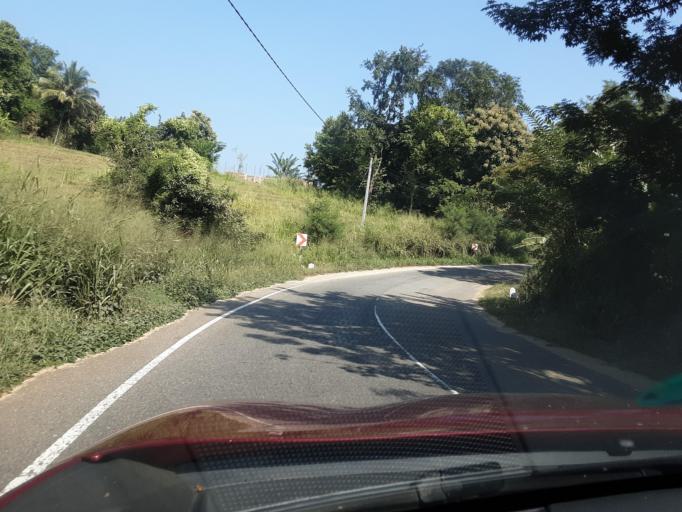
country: LK
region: Uva
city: Badulla
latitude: 7.1644
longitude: 81.0522
